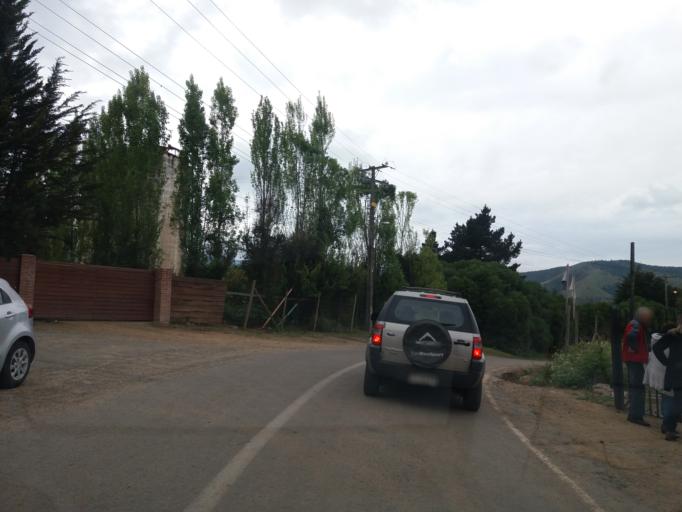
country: CL
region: Valparaiso
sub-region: Provincia de Quillota
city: Quillota
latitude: -32.8926
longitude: -71.3205
